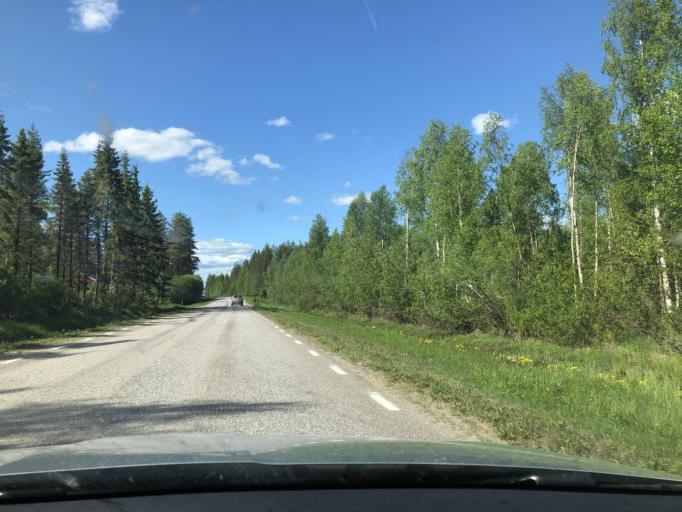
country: SE
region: Norrbotten
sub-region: Kalix Kommun
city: Kalix
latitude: 65.9668
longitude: 23.1467
